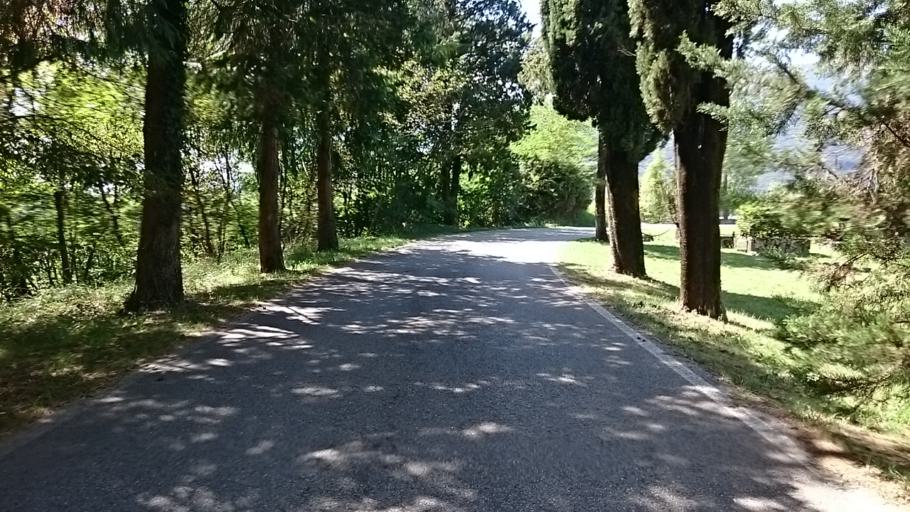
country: IT
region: Veneto
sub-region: Provincia di Treviso
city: Cison di Valmarino
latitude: 45.9608
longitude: 12.1429
